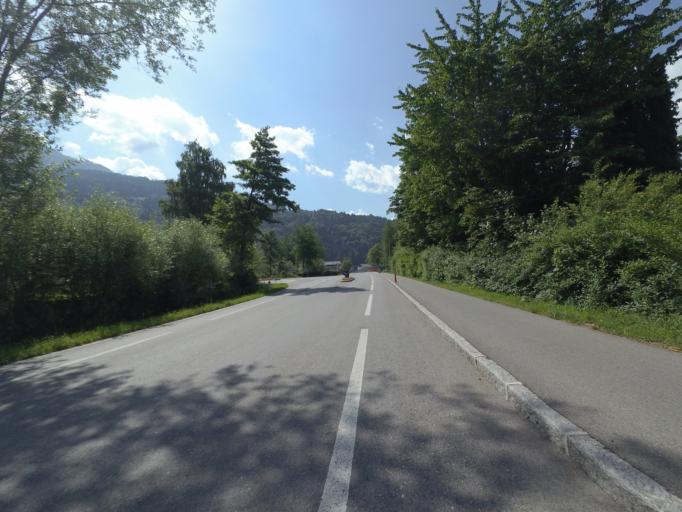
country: AT
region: Carinthia
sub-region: Politischer Bezirk Villach Land
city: Ferndorf
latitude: 46.7735
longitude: 13.6451
